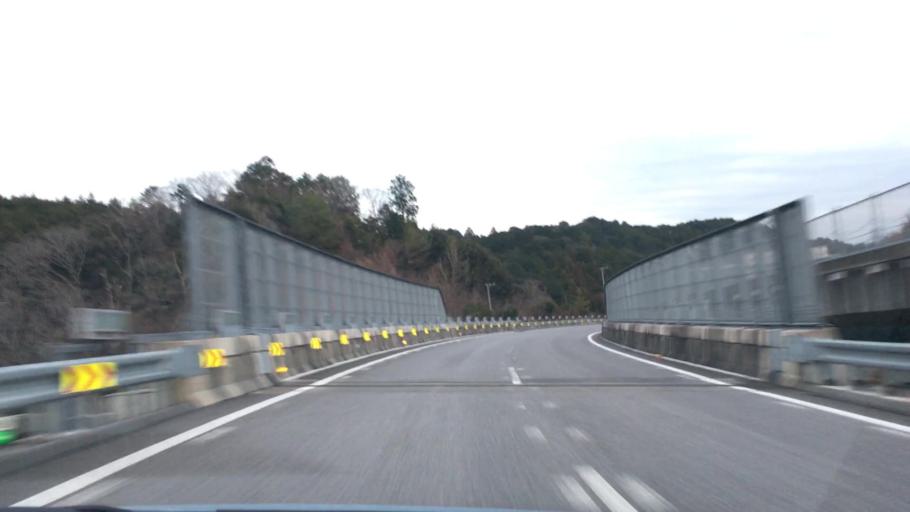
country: JP
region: Aichi
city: Shinshiro
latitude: 34.8931
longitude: 137.6493
